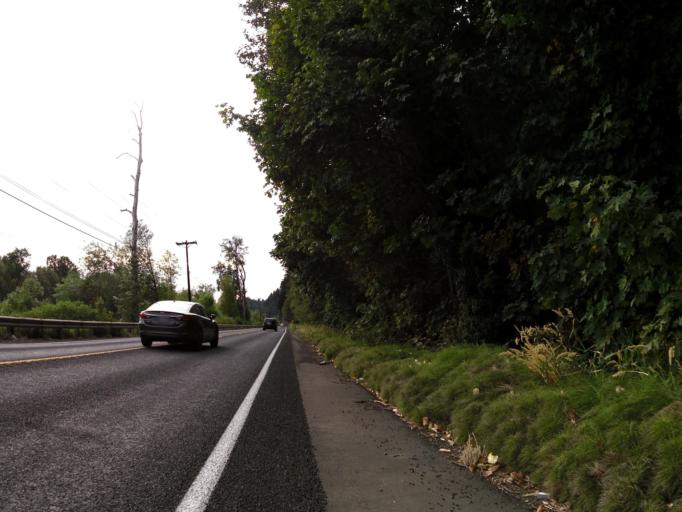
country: US
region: Washington
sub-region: Cowlitz County
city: West Longview
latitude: 46.1886
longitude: -123.1024
